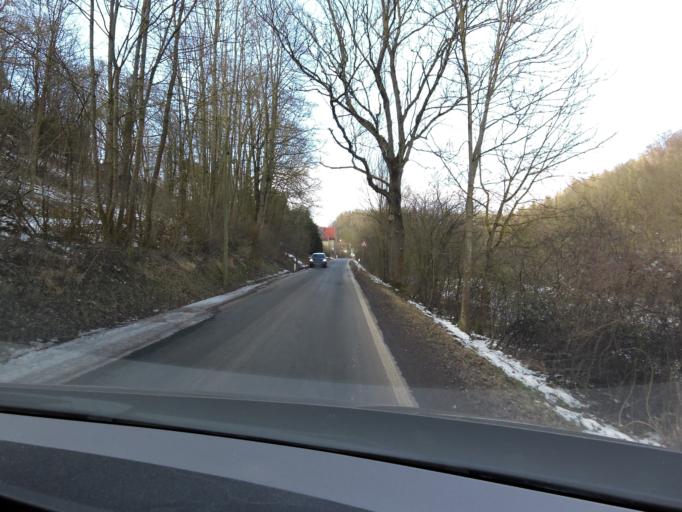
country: DE
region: Thuringia
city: Wolfsburg-Unkeroda
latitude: 50.8853
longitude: 10.2585
